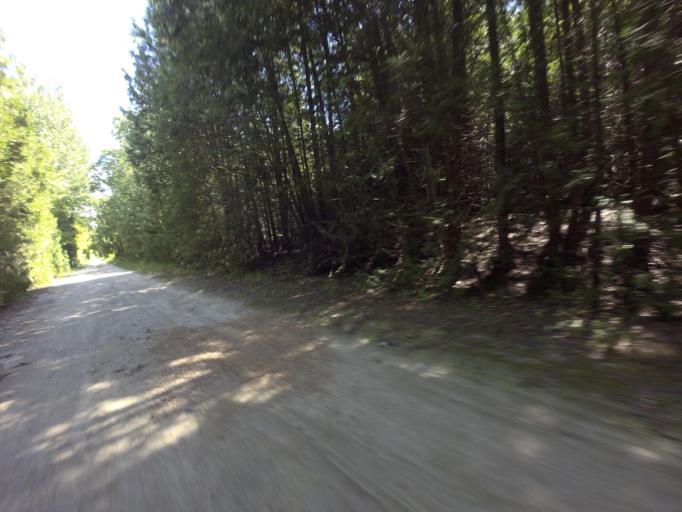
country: CA
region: Ontario
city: Orangeville
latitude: 43.7764
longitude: -80.1100
